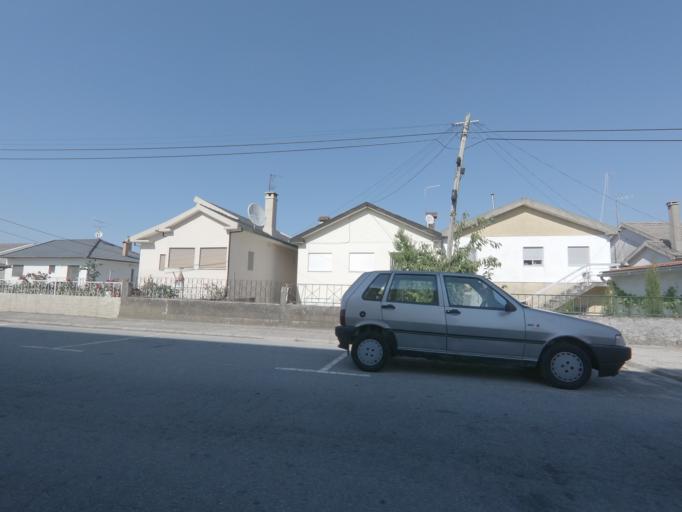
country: PT
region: Viseu
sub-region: Moimenta da Beira
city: Moimenta da Beira
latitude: 40.9845
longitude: -7.6202
